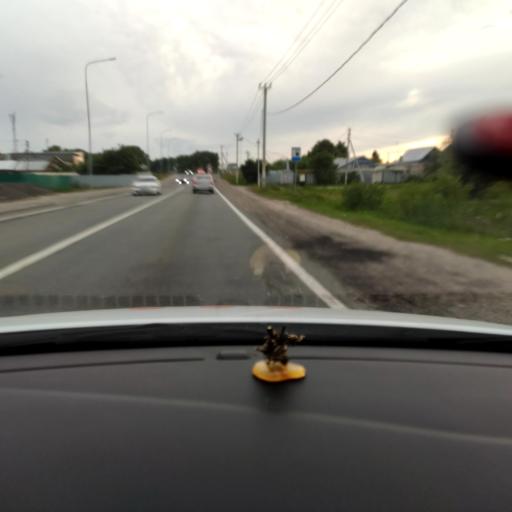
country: RU
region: Tatarstan
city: Aysha
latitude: 55.8708
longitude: 48.6348
